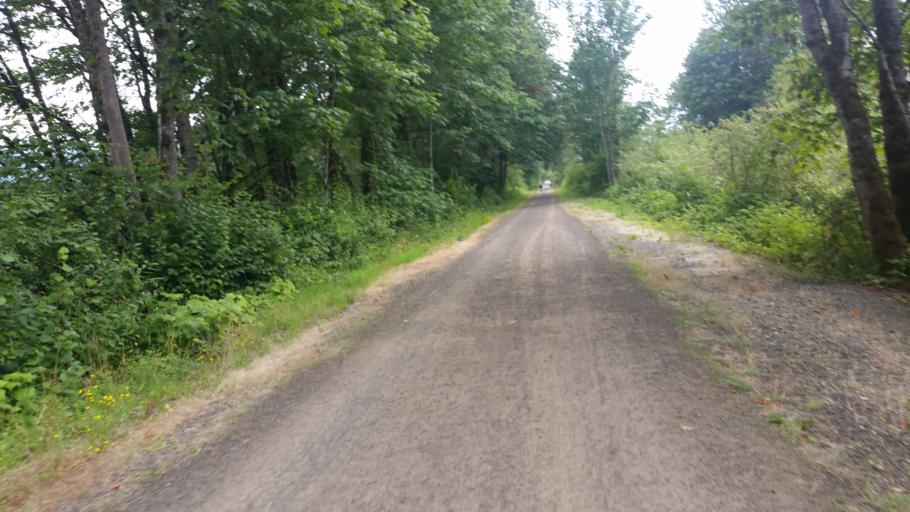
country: US
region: Washington
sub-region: King County
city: Snoqualmie
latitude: 47.5269
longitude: -121.8047
